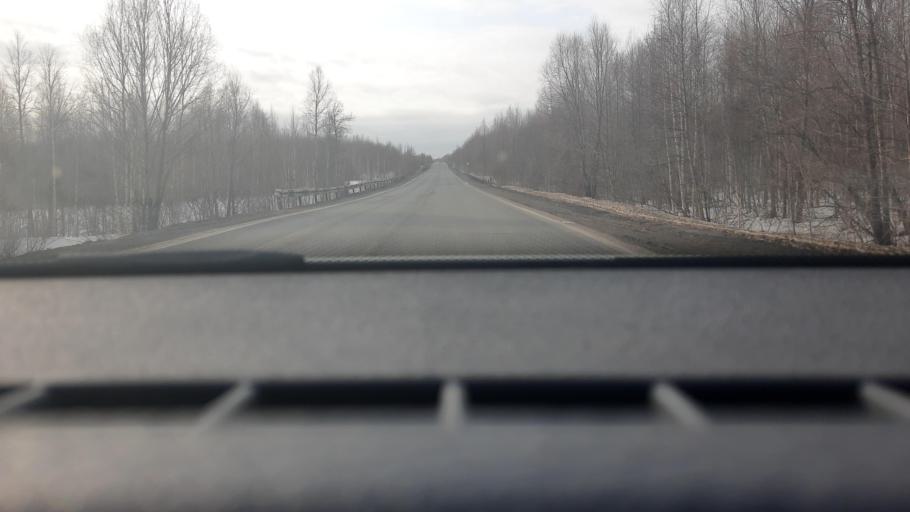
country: RU
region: Chelyabinsk
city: Asha
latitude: 54.9273
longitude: 57.2893
